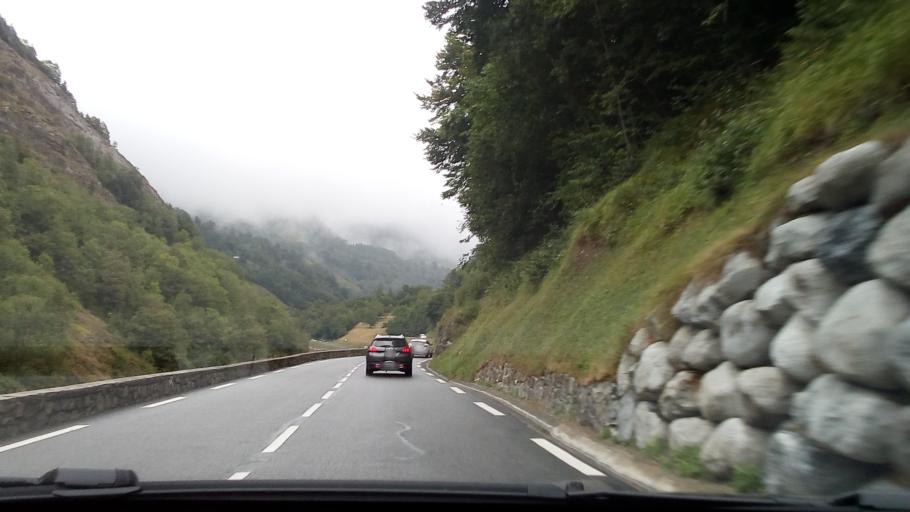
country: FR
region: Midi-Pyrenees
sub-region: Departement des Hautes-Pyrenees
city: Luz-Saint-Sauveur
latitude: 42.8846
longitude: 0.0425
